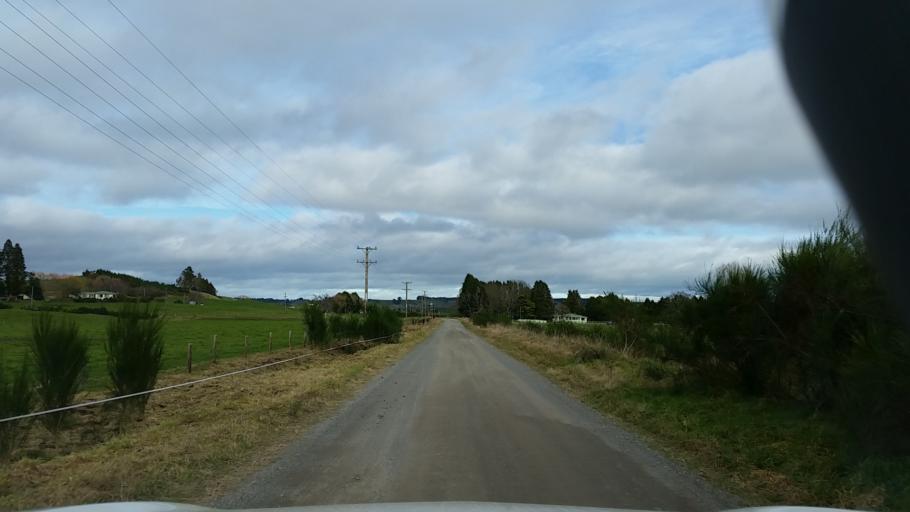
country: NZ
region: Bay of Plenty
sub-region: Whakatane District
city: Murupara
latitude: -38.2895
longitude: 176.5466
